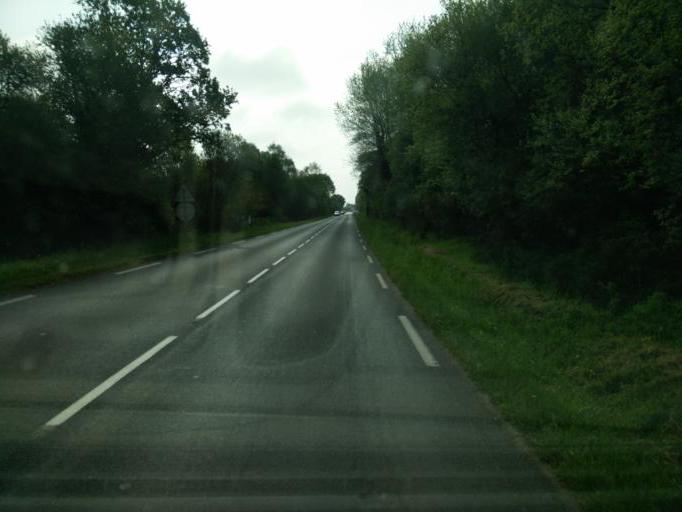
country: FR
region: Brittany
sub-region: Departement du Finistere
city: Moelan-sur-Mer
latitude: 47.8169
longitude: -3.6505
